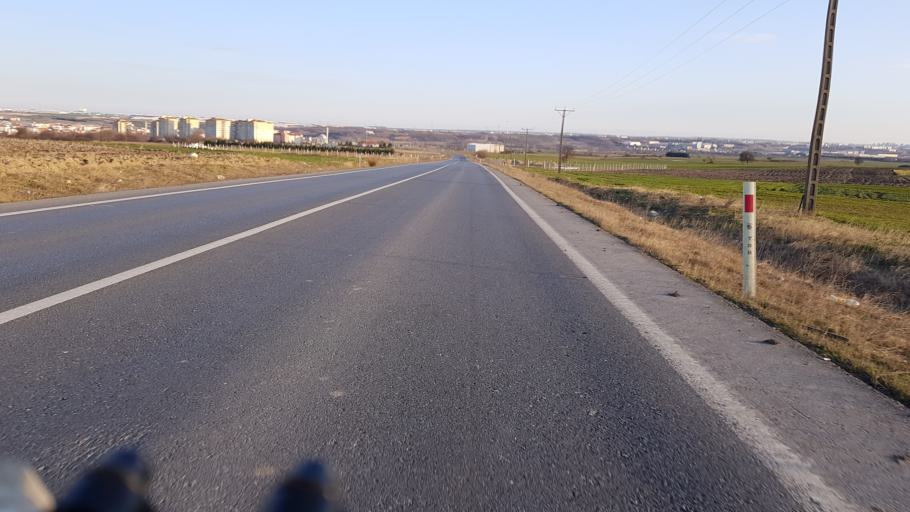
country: TR
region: Tekirdag
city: Velimese
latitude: 41.2596
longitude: 27.8591
